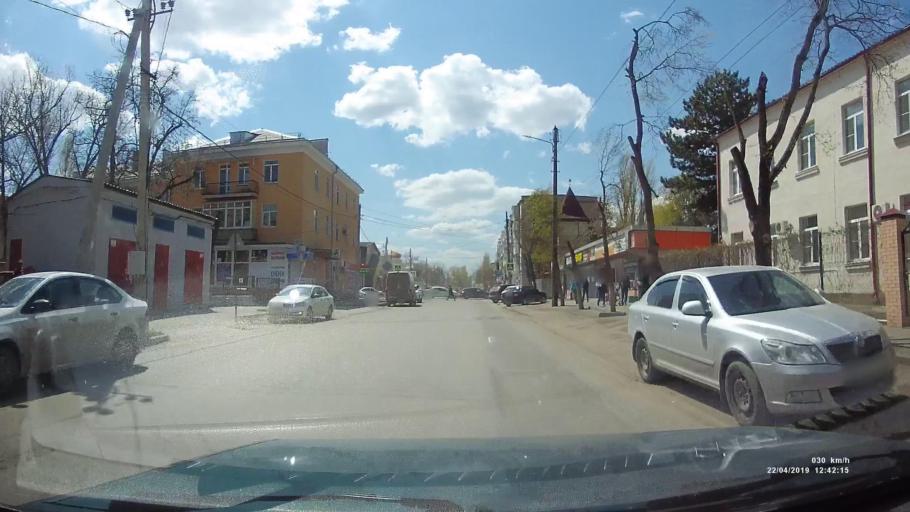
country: RU
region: Rostov
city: Azov
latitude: 47.1054
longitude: 39.4274
